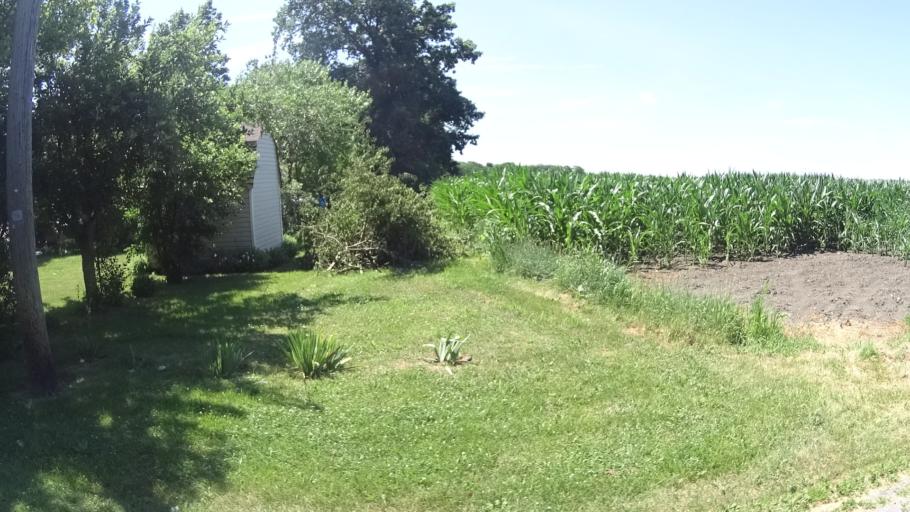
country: US
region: Ohio
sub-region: Ottawa County
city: Port Clinton
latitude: 41.4467
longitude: -82.8454
